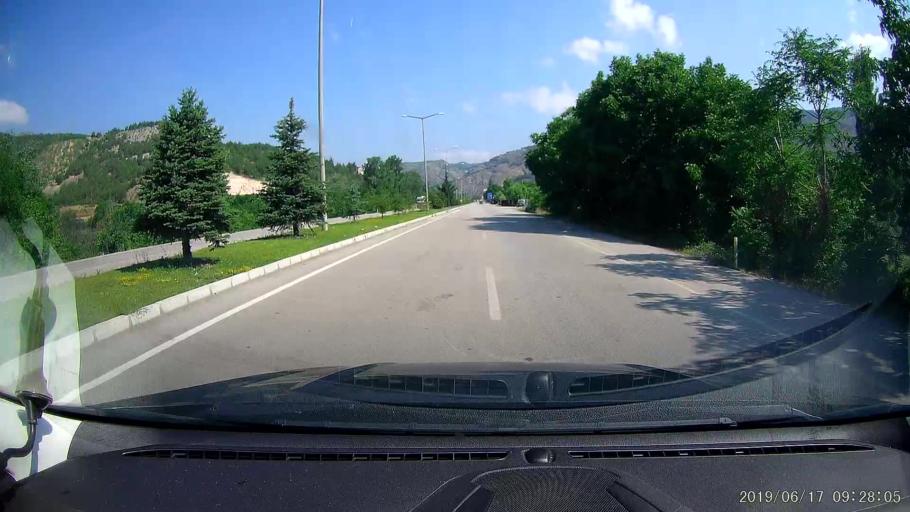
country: TR
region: Amasya
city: Amasya
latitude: 40.6842
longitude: 35.8232
